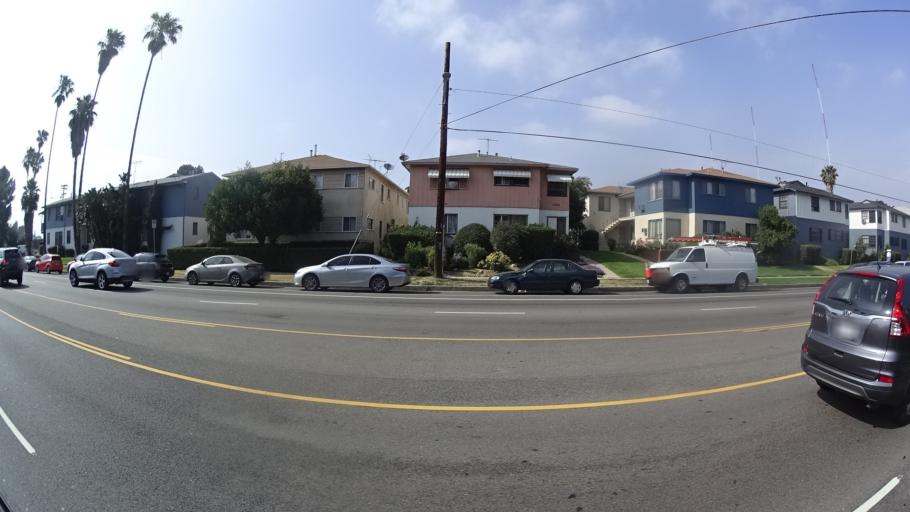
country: US
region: California
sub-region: Los Angeles County
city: North Hollywood
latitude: 34.1720
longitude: -118.4123
